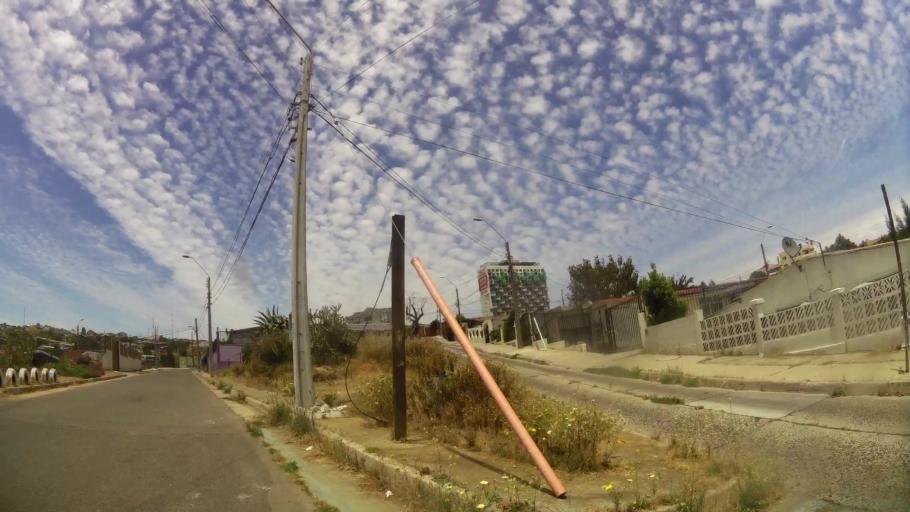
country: CL
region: Valparaiso
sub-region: Provincia de Valparaiso
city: Vina del Mar
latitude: -33.0459
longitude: -71.5762
